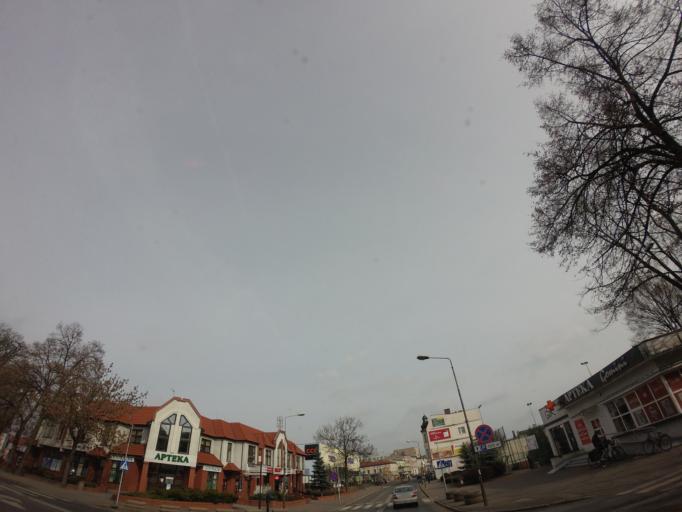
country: PL
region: West Pomeranian Voivodeship
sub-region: Powiat walecki
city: Walcz
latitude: 53.2718
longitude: 16.4687
